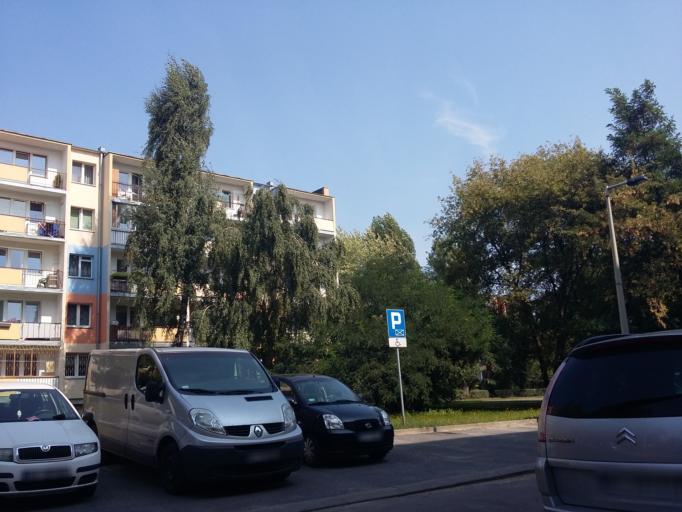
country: PL
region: Lodz Voivodeship
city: Lodz
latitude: 51.7466
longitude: 19.4144
